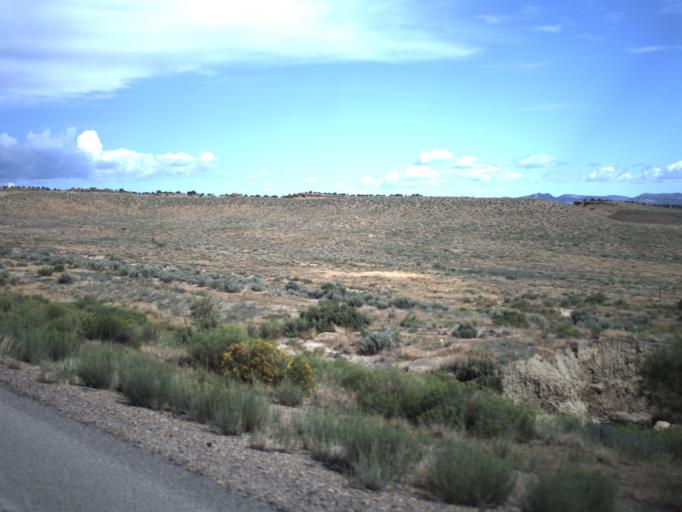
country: US
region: Utah
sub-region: Carbon County
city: Wellington
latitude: 39.5406
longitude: -110.6078
